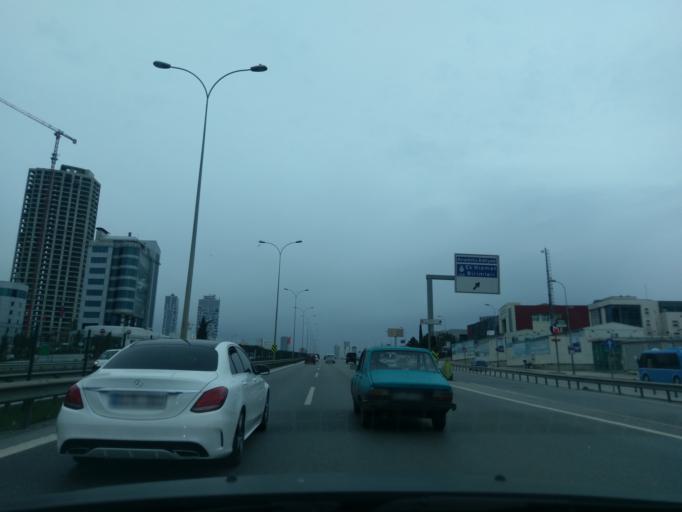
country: TR
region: Istanbul
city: Maltepe
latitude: 40.9177
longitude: 29.1750
